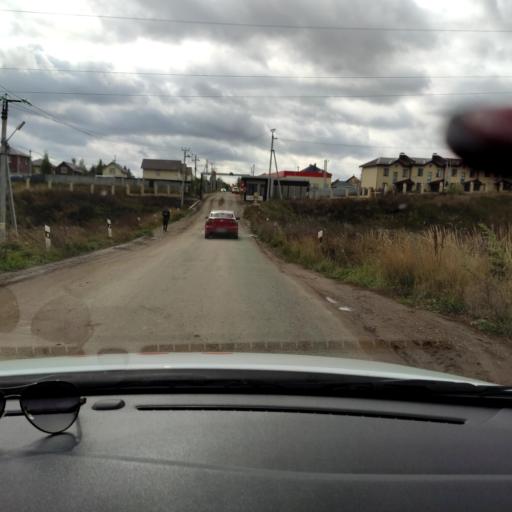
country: RU
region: Tatarstan
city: Stolbishchi
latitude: 55.7262
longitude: 49.3145
